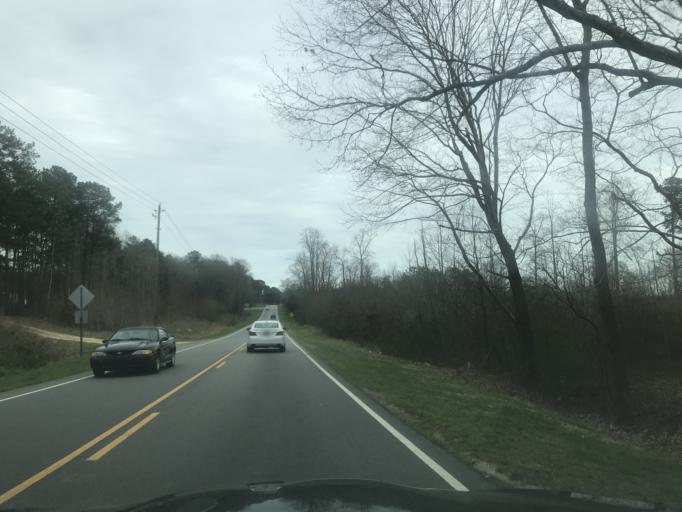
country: US
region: North Carolina
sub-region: Franklin County
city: Louisburg
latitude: 36.0867
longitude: -78.3569
